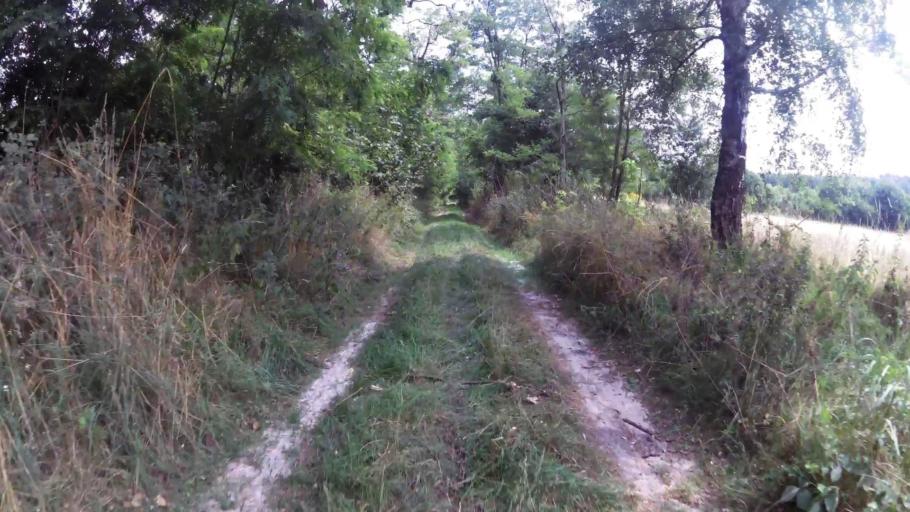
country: PL
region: West Pomeranian Voivodeship
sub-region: Powiat gryfinski
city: Chojna
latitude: 52.9036
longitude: 14.5141
